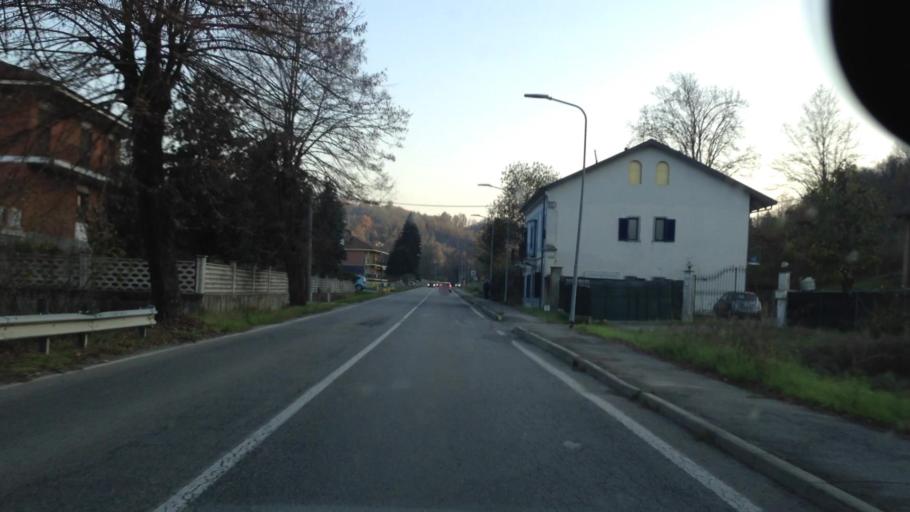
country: IT
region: Piedmont
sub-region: Provincia di Torino
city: Cavagnolo
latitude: 45.1487
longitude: 8.0538
